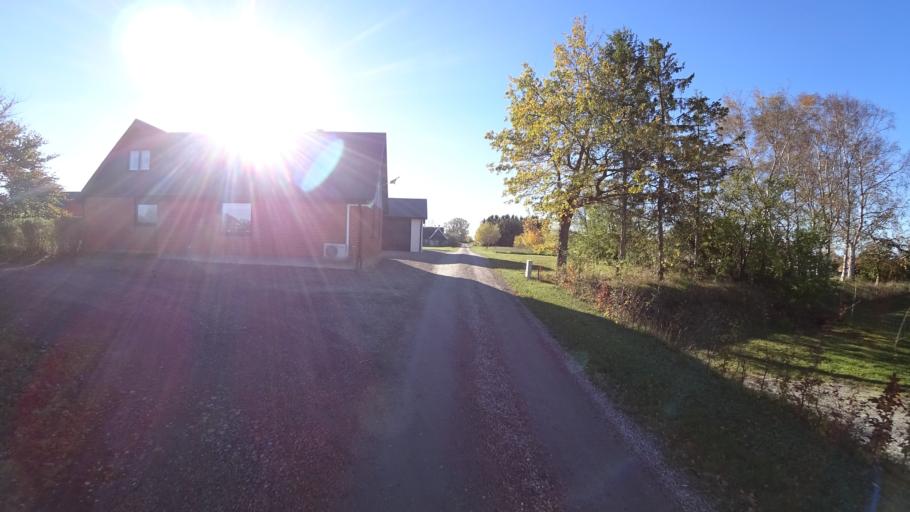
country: SE
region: Skane
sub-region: Svedala Kommun
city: Klagerup
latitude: 55.6498
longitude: 13.2899
